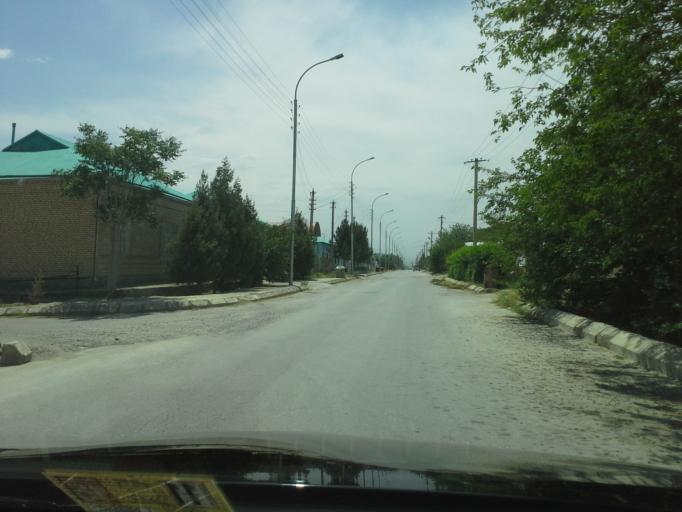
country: TM
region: Ahal
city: Ashgabat
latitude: 37.9983
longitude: 58.4169
